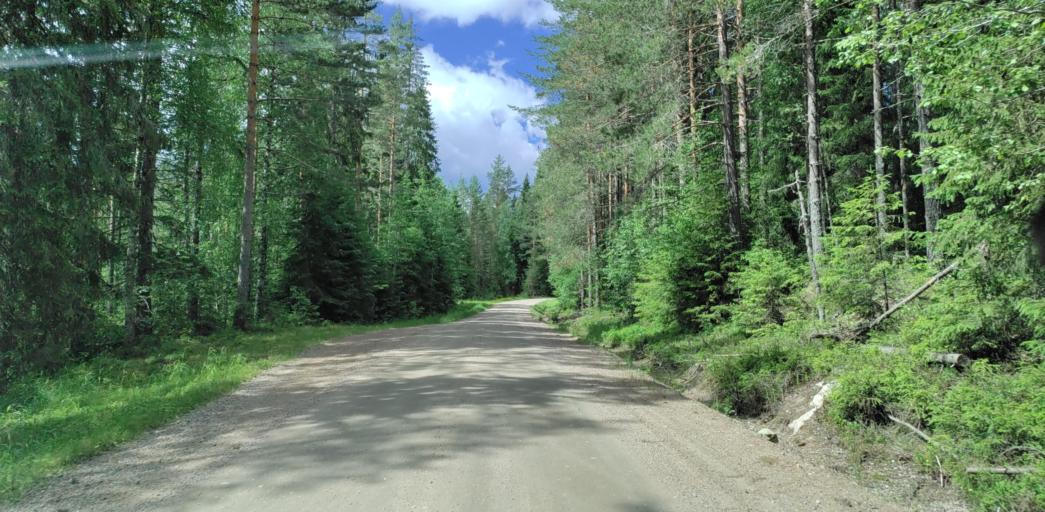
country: SE
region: Vaermland
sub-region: Hagfors Kommun
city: Ekshaerad
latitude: 60.0977
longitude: 13.3957
